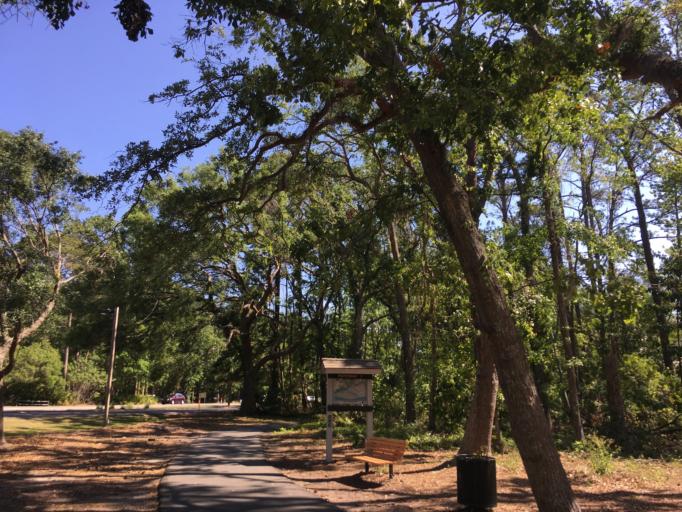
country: US
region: South Carolina
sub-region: Beaufort County
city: Hilton Head Island
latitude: 32.1600
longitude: -80.7514
